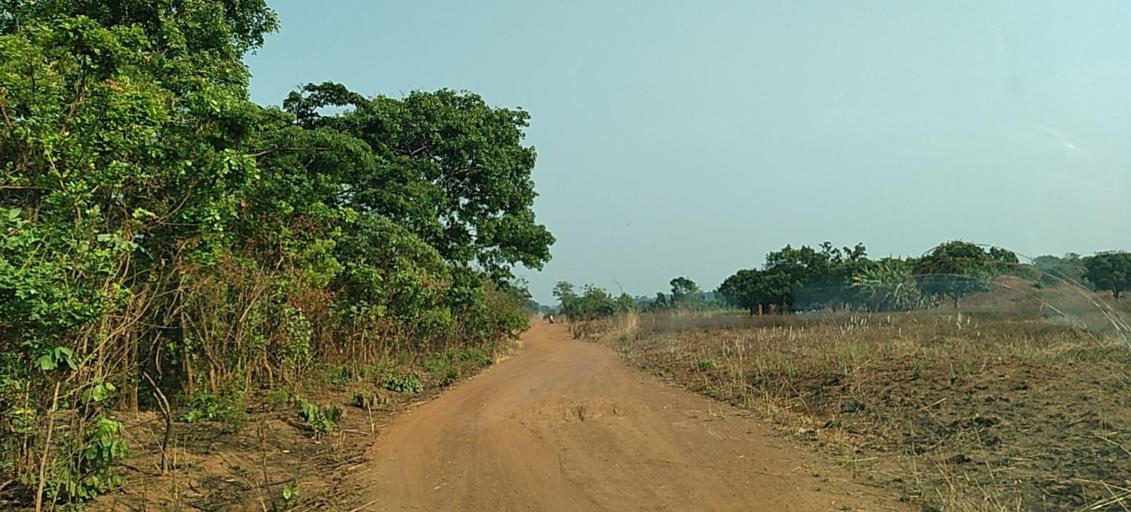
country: ZM
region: Copperbelt
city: Chingola
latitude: -12.8338
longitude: 27.5413
